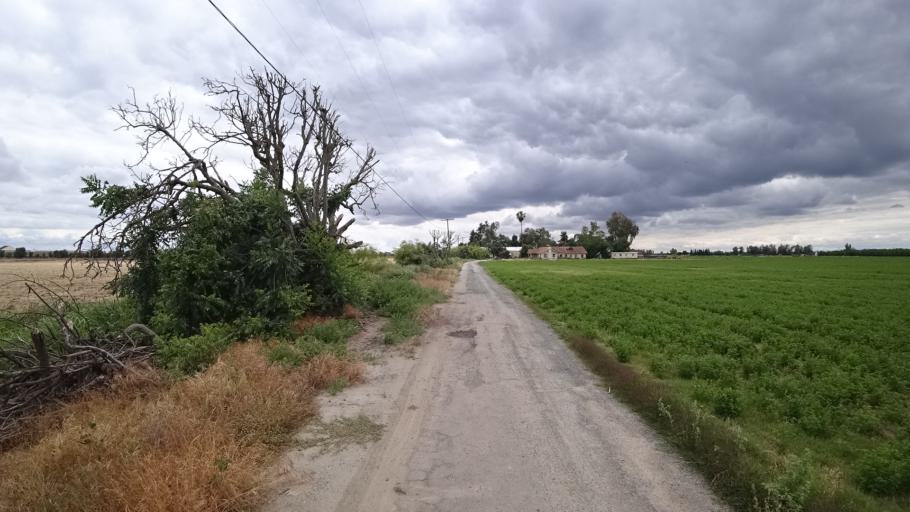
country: US
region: California
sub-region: Kings County
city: Armona
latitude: 36.3242
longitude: -119.6820
